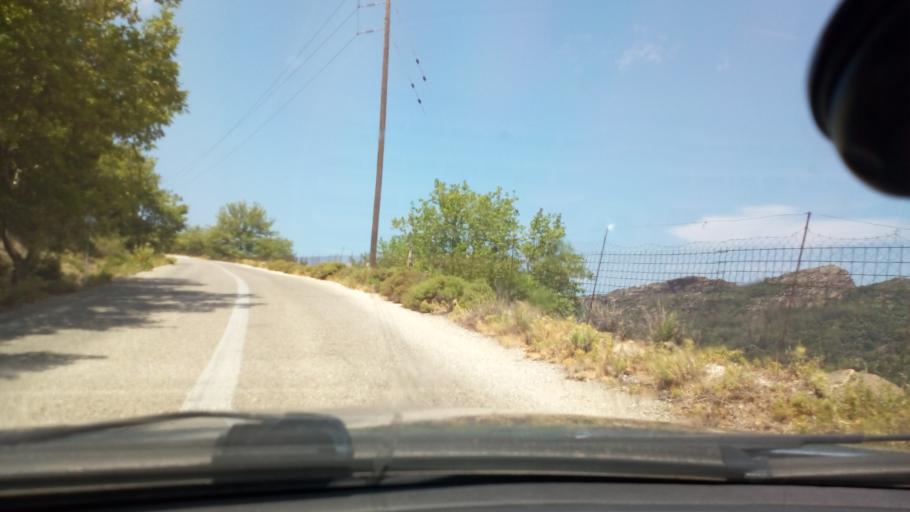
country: GR
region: North Aegean
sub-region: Nomos Samou
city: Agios Kirykos
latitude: 37.6361
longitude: 26.2582
